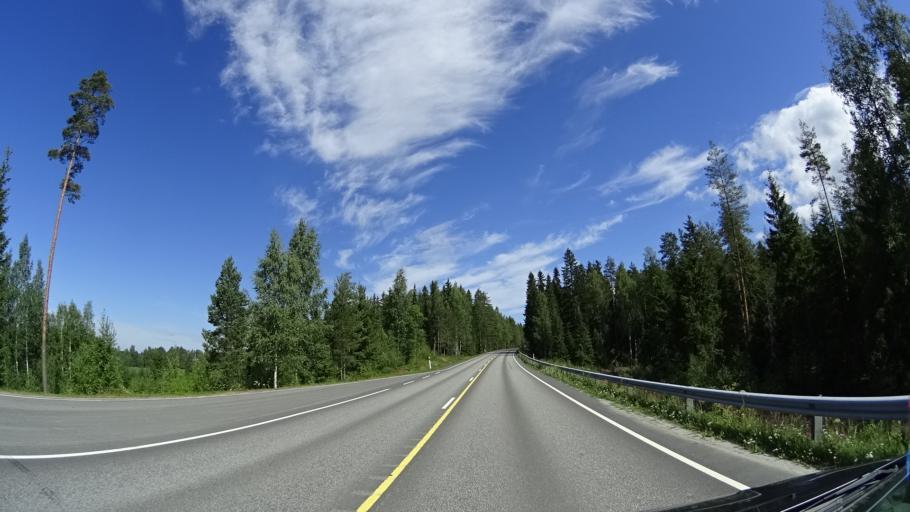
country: FI
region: Pirkanmaa
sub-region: Luoteis-Pirkanmaa
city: Kihnioe
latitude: 62.1083
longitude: 23.1012
